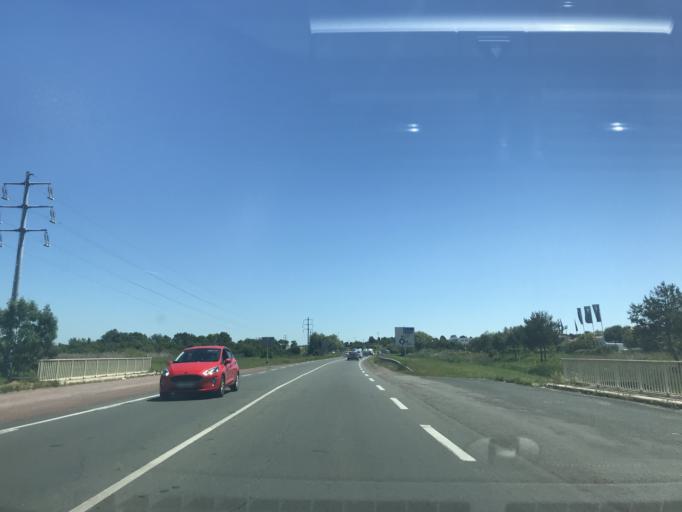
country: FR
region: Poitou-Charentes
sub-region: Departement de la Charente-Maritime
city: Saint-Georges-de-Didonne
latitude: 45.6185
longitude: -0.9908
